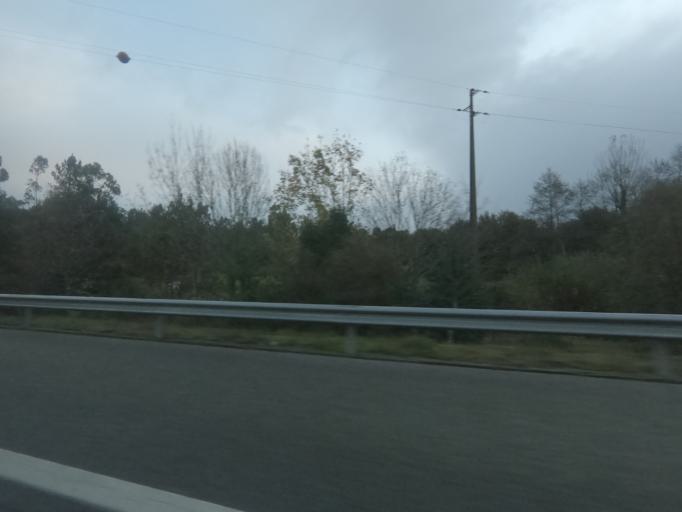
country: PT
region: Braga
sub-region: Barcelos
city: Galegos
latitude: 41.6222
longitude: -8.5558
